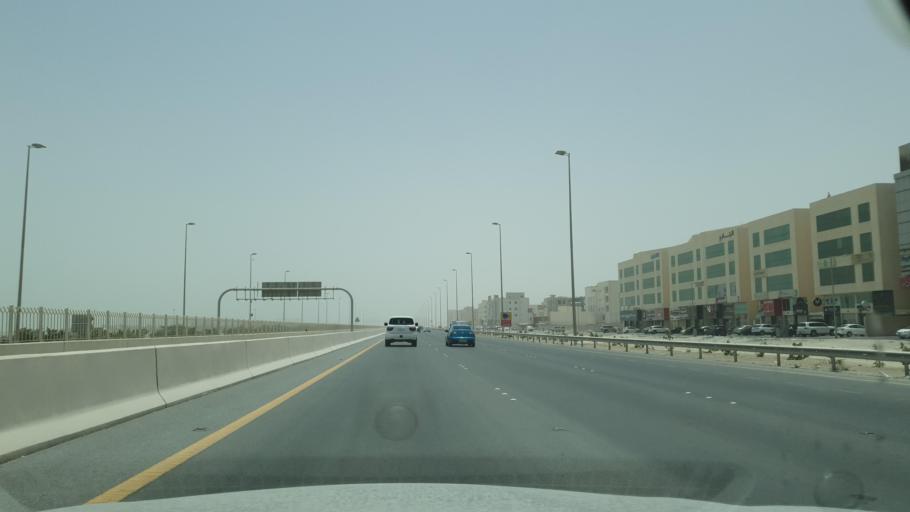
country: BH
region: Muharraq
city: Al Hadd
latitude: 26.2827
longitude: 50.6473
